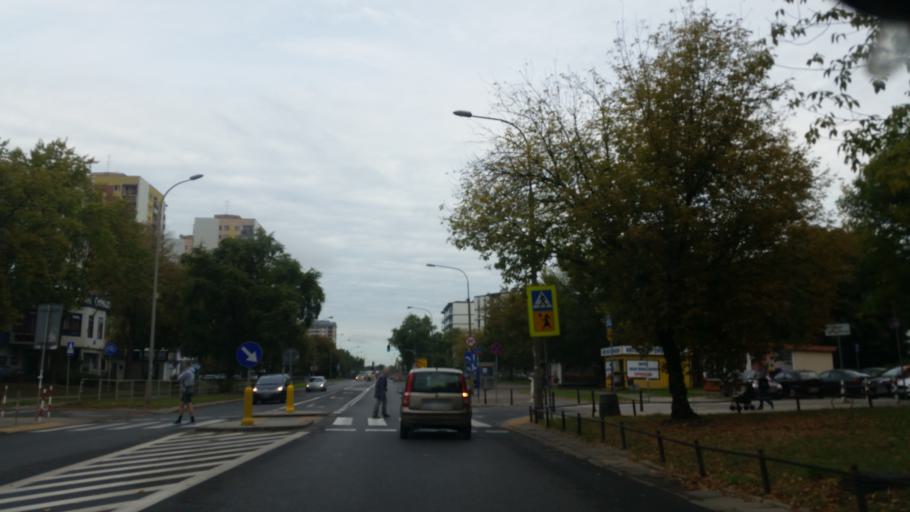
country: PL
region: Masovian Voivodeship
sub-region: Warszawa
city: Bielany
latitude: 52.2757
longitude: 20.9233
